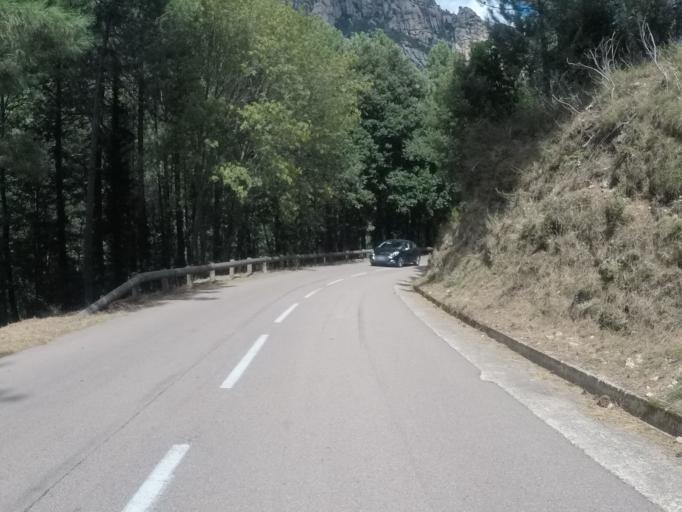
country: FR
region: Corsica
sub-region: Departement de la Corse-du-Sud
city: Zonza
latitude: 41.8113
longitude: 9.2456
